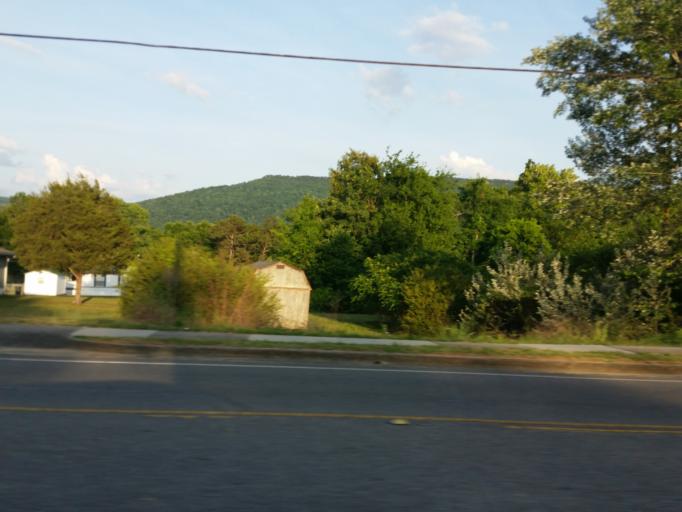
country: US
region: Georgia
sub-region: Dade County
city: Trenton
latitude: 34.8610
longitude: -85.5175
